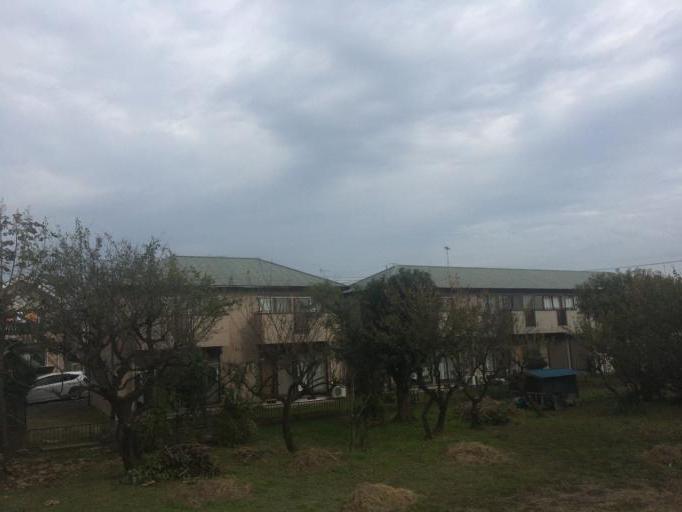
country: JP
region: Tokyo
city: Fussa
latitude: 35.7062
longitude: 139.3586
